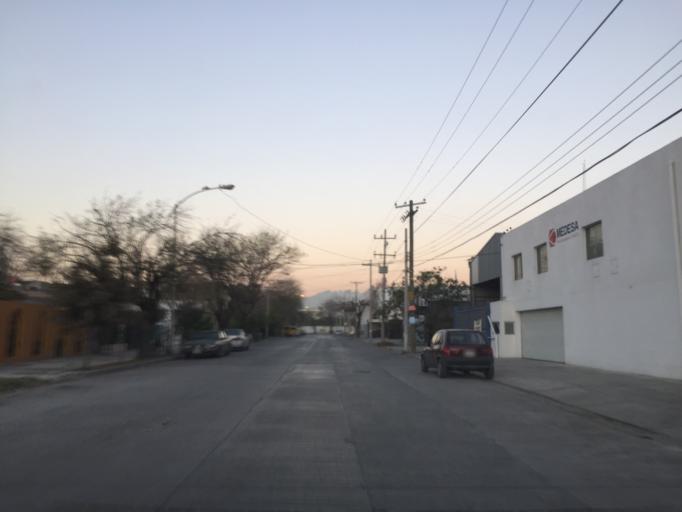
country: MX
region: Nuevo Leon
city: Guadalupe
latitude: 25.6994
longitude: -100.2211
